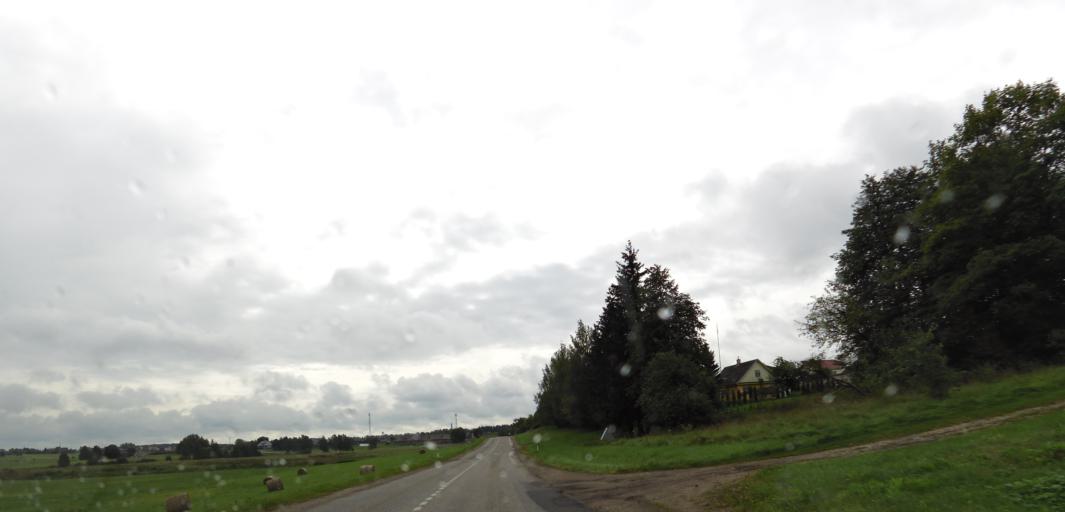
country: LT
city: Moletai
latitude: 55.2350
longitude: 25.3866
